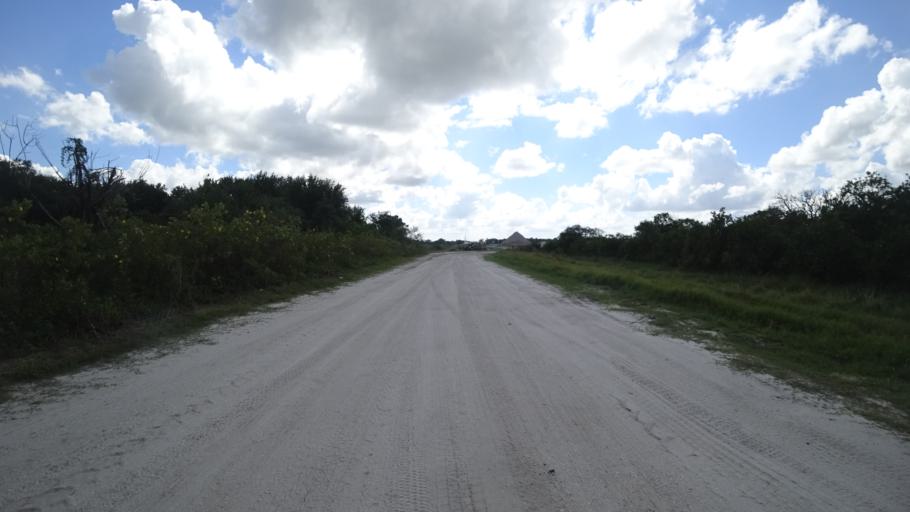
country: US
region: Florida
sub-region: Sarasota County
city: The Meadows
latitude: 27.4600
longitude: -82.3713
